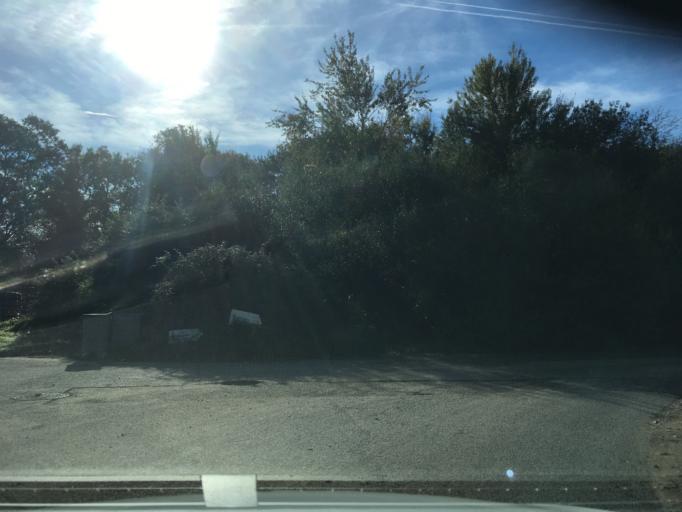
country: FR
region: Aquitaine
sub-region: Departement des Pyrenees-Atlantiques
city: Idron
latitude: 43.3163
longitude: -0.3082
